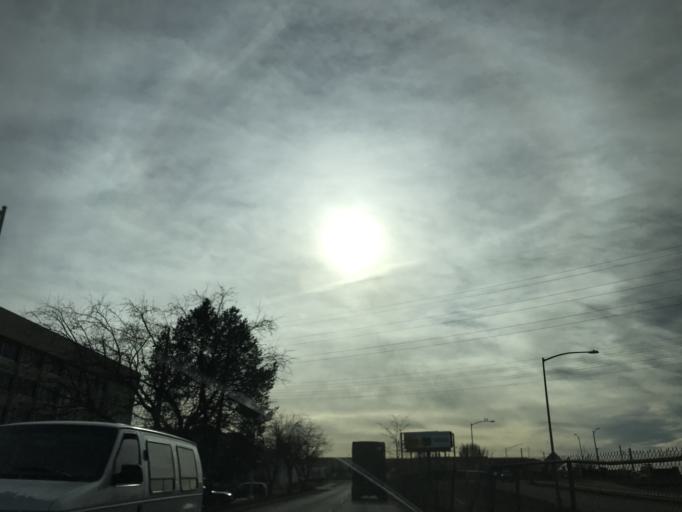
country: US
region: Colorado
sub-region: Adams County
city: Commerce City
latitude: 39.7738
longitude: -104.9026
